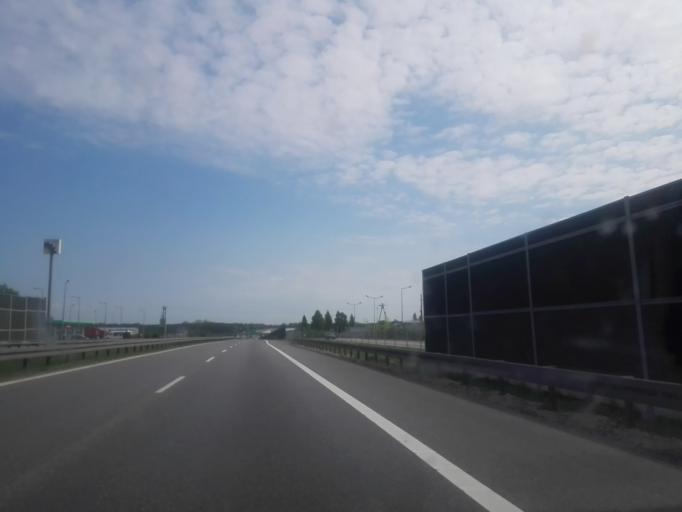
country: PL
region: Masovian Voivodeship
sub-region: Powiat zyrardowski
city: Radziejowice
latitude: 51.9923
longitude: 20.5450
